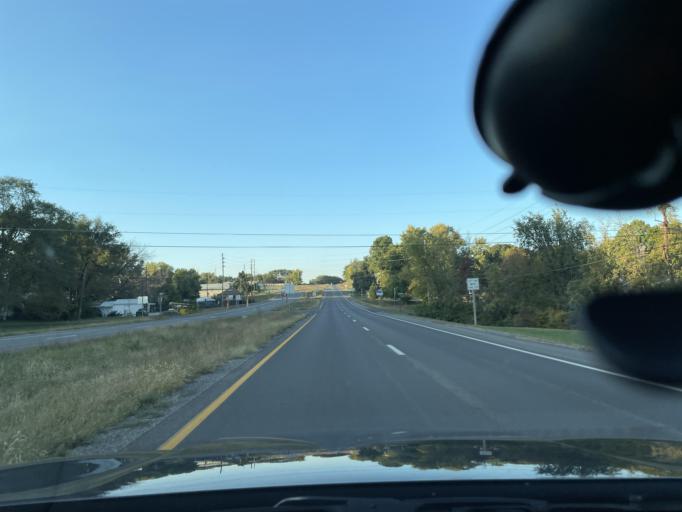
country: US
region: Missouri
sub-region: Andrew County
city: Country Club Village
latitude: 39.8117
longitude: -94.8406
